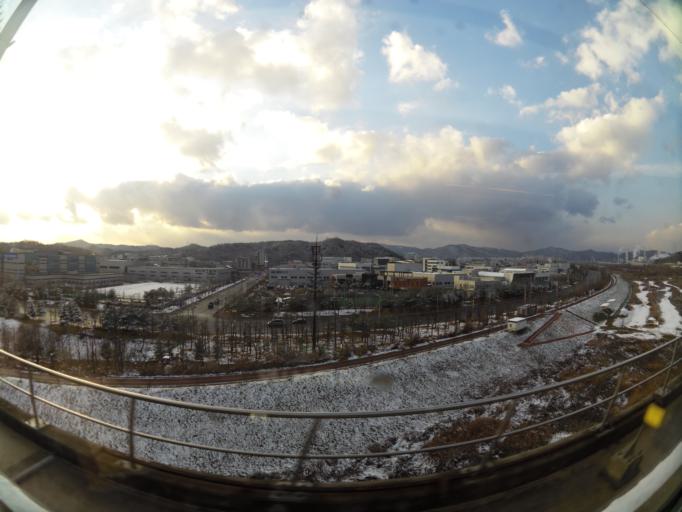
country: KR
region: Daejeon
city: Songgang-dong
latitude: 36.4172
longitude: 127.4157
